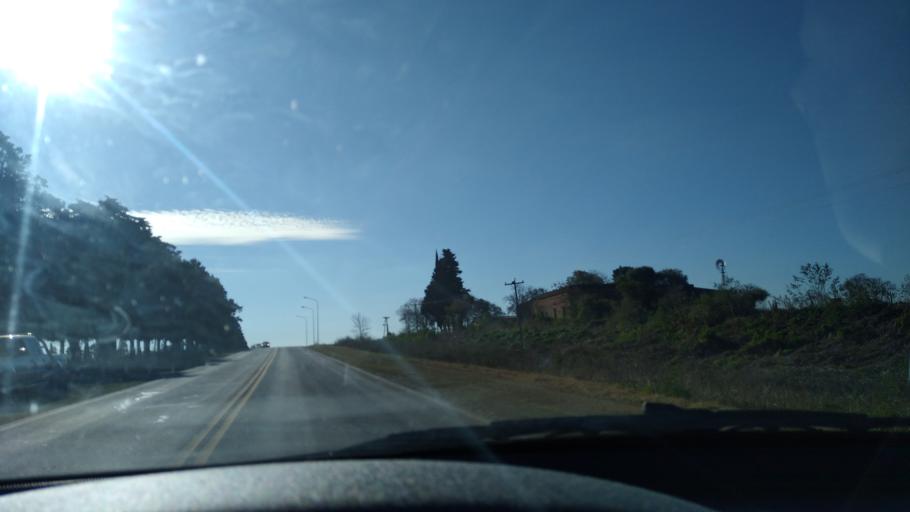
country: AR
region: Entre Rios
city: Aranguren
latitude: -32.4158
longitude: -60.3183
